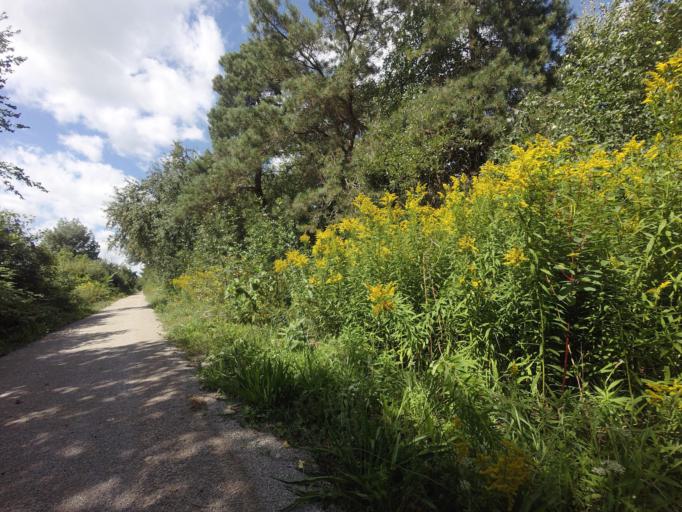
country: CA
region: Ontario
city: Huron East
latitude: 43.6272
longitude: -81.1708
